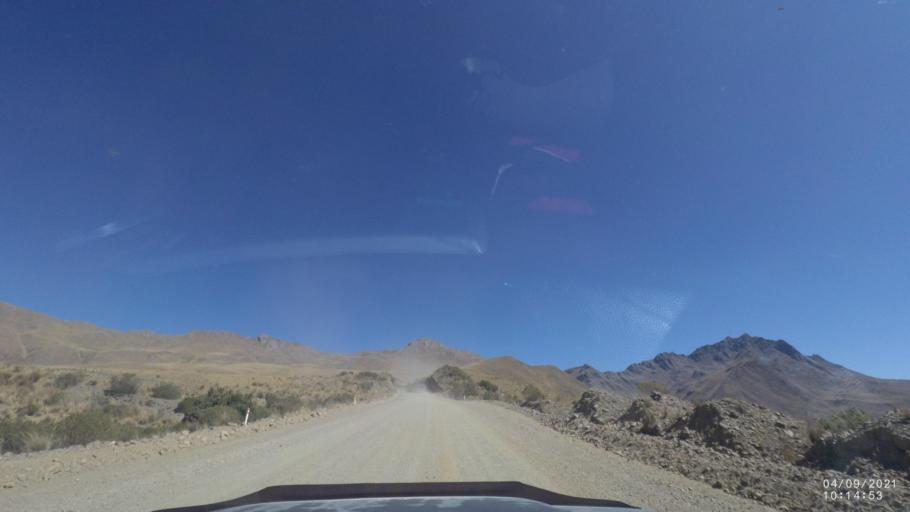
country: BO
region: Cochabamba
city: Sipe Sipe
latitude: -17.3277
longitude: -66.4117
